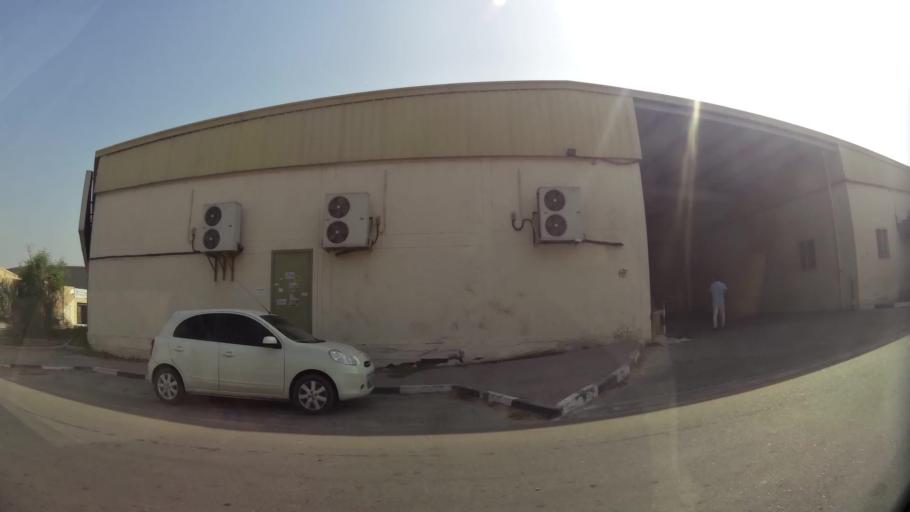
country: AE
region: Ash Shariqah
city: Sharjah
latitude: 25.2946
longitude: 55.3921
